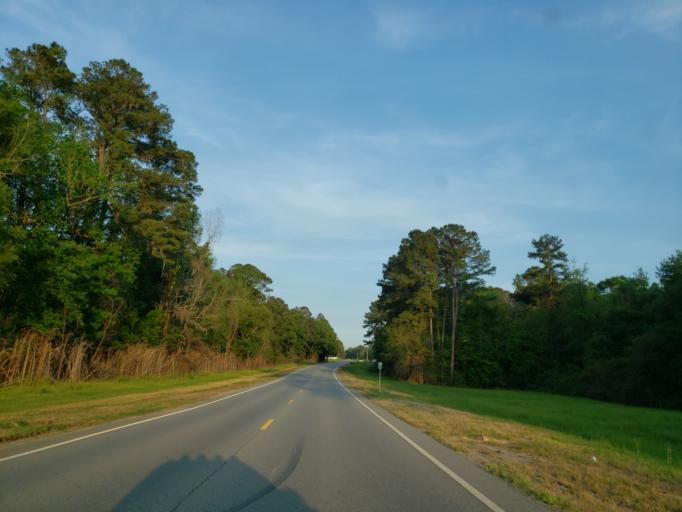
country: US
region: Georgia
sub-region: Lowndes County
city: Hahira
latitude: 30.9973
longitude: -83.4423
